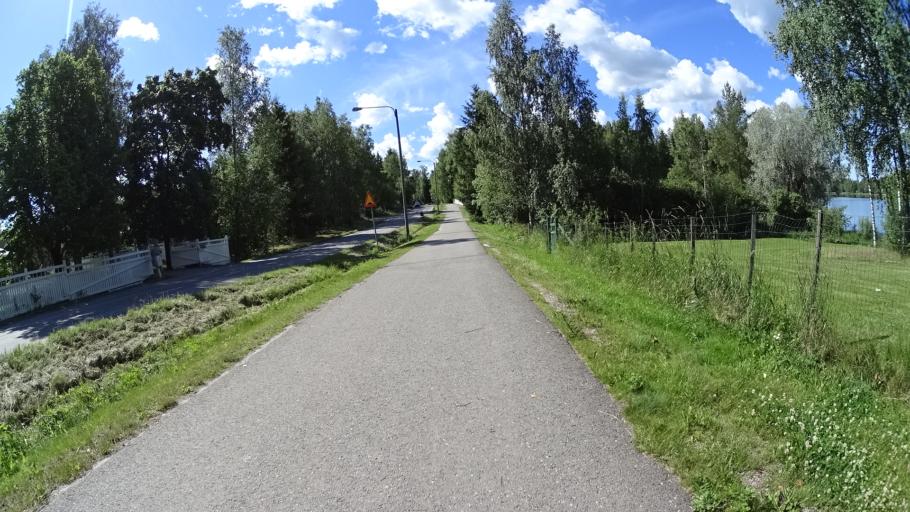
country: FI
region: Uusimaa
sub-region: Helsinki
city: Kirkkonummi
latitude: 60.2787
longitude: 24.4404
